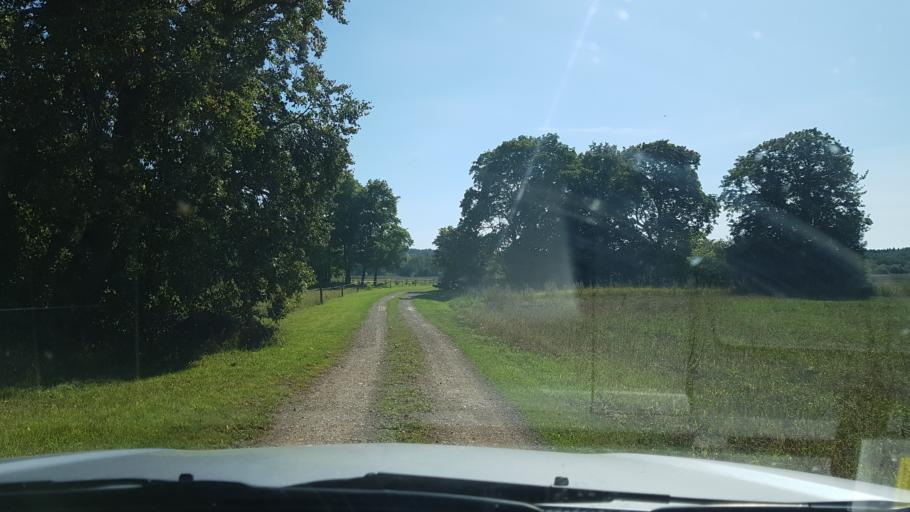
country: EE
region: Ida-Virumaa
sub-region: Sillamaee linn
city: Sillamae
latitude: 59.3938
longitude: 27.8464
